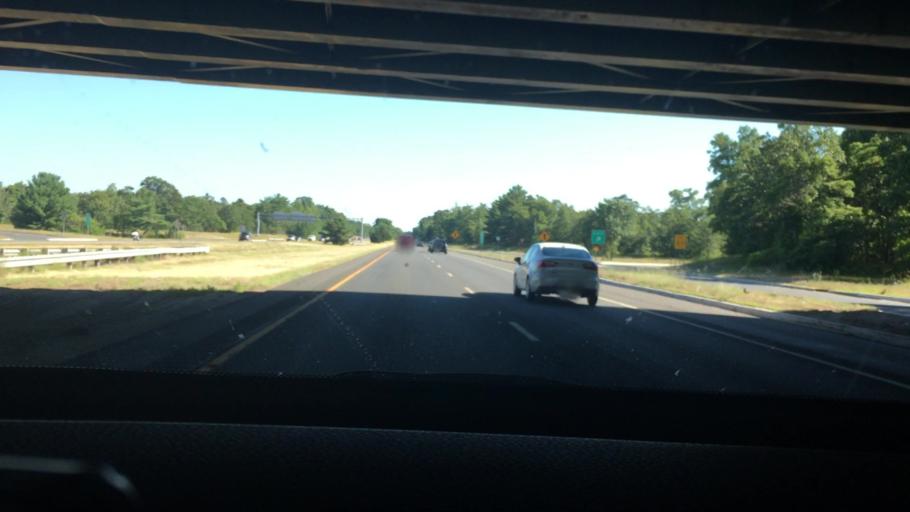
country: US
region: New Jersey
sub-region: Cumberland County
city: Vineland
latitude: 39.4883
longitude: -75.0714
